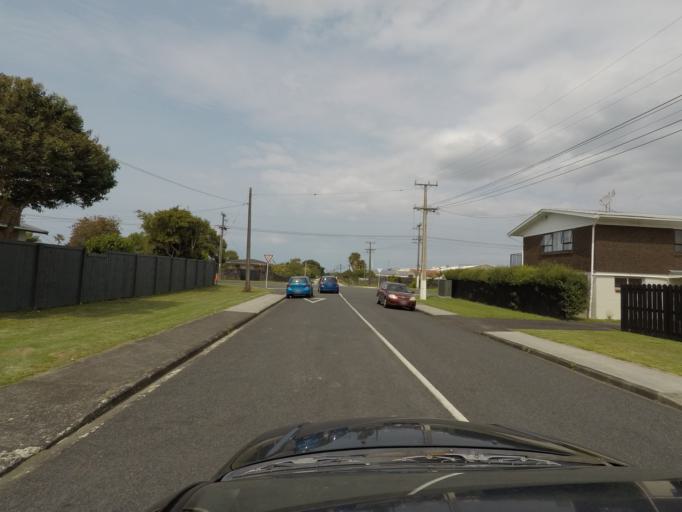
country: NZ
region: Auckland
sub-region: Auckland
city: Rosebank
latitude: -36.8288
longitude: 174.6461
